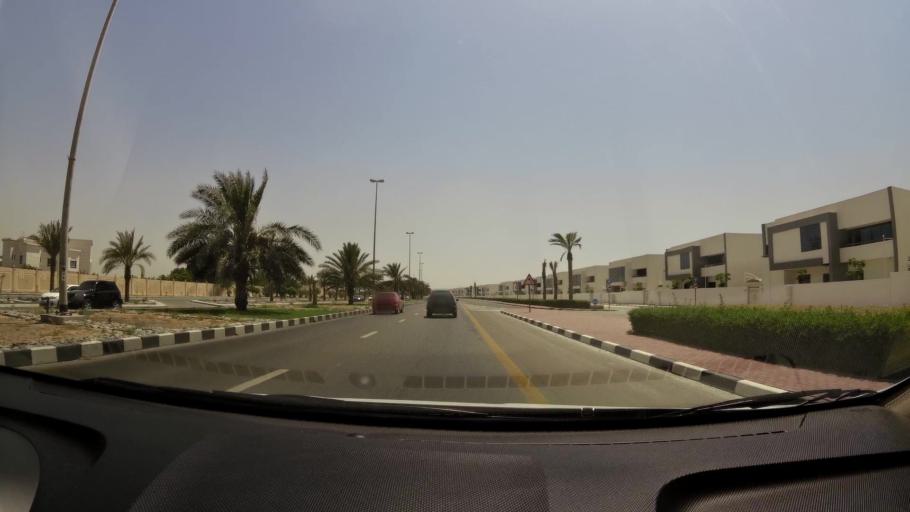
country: AE
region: Ajman
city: Ajman
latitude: 25.4228
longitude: 55.4936
